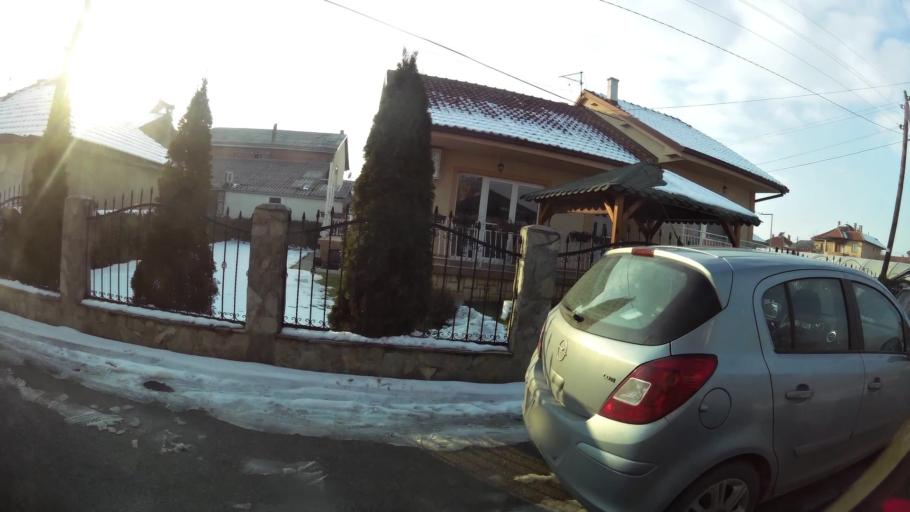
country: MK
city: Creshevo
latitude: 42.0305
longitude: 21.5193
